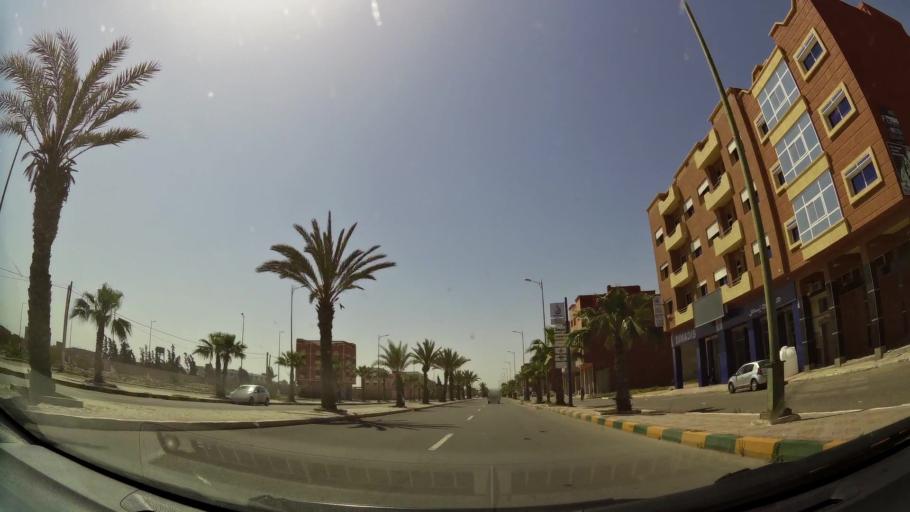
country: MA
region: Souss-Massa-Draa
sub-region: Inezgane-Ait Mellou
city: Inezgane
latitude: 30.3192
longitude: -9.5032
